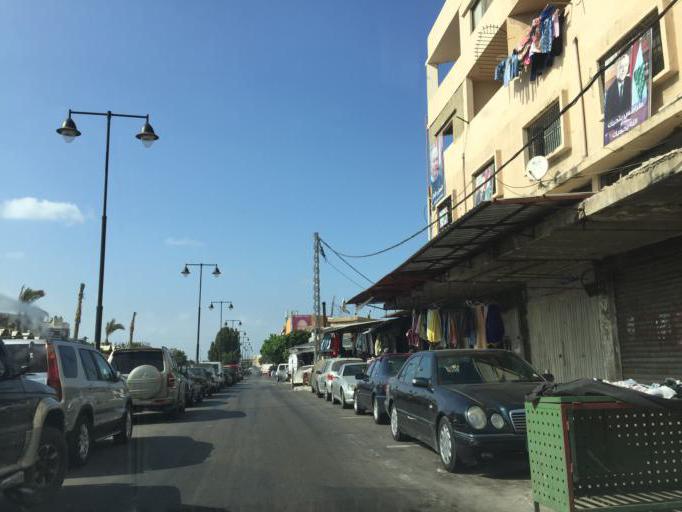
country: LB
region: Liban-Nord
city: Tripoli
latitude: 34.4388
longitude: 35.8474
